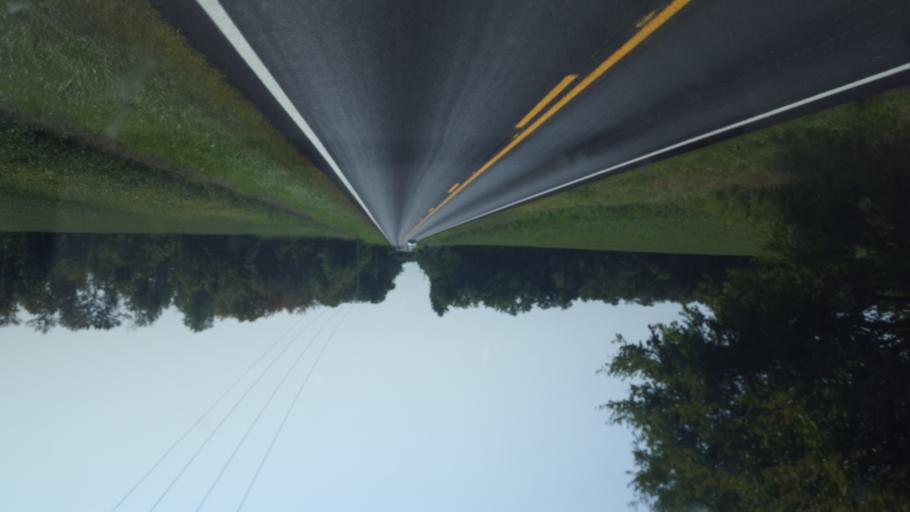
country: US
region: Ohio
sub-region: Sandusky County
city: Bellville
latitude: 40.5763
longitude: -82.5719
